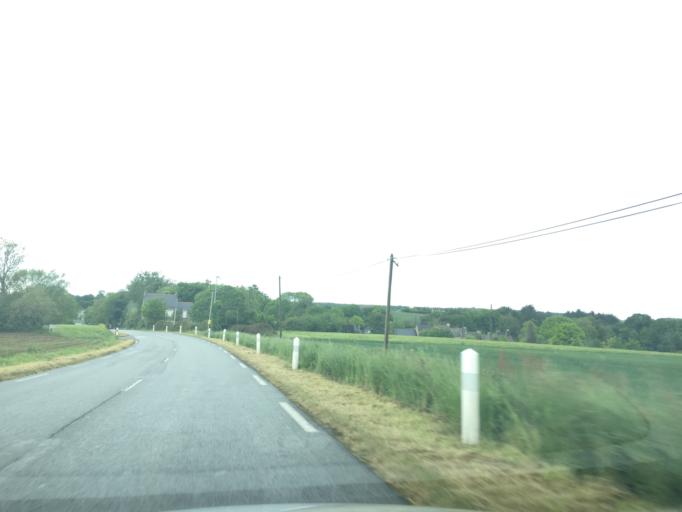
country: FR
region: Brittany
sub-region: Departement des Cotes-d'Armor
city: Ploubalay
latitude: 48.5842
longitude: -2.1208
